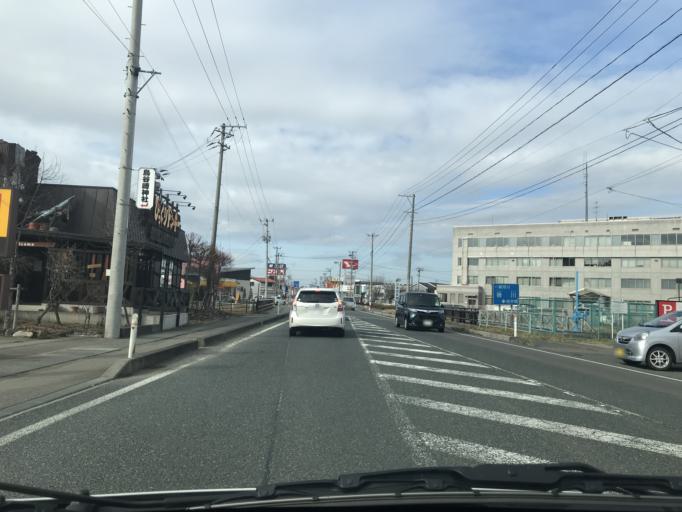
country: JP
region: Iwate
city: Hanamaki
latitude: 39.3909
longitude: 141.1242
